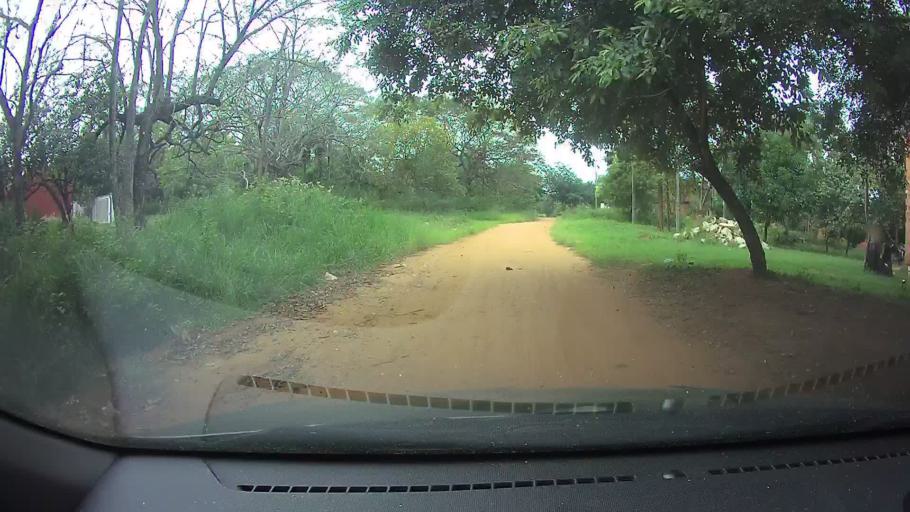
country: PY
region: Central
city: Limpio
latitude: -25.2374
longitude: -57.4591
